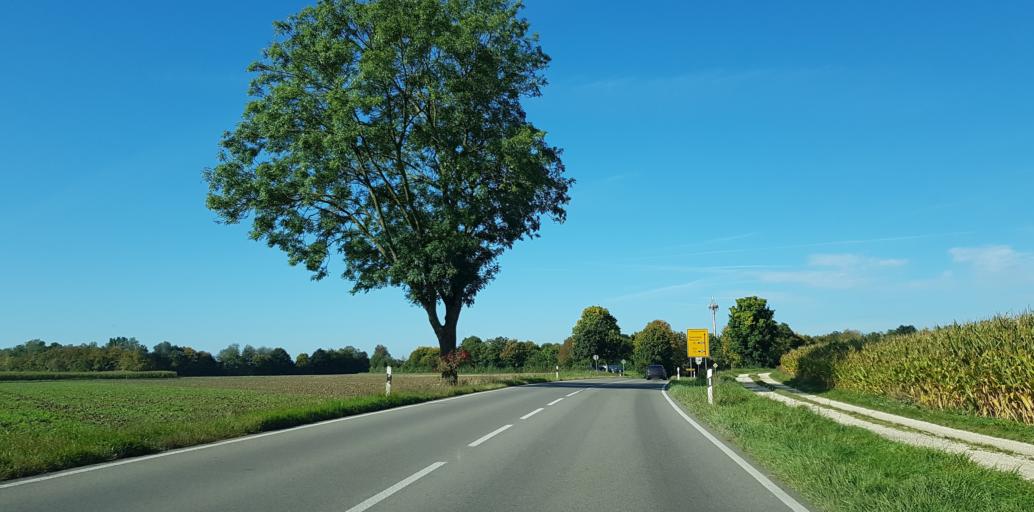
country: DE
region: Baden-Wuerttemberg
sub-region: Tuebingen Region
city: Huttisheim
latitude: 48.3298
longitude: 9.9465
